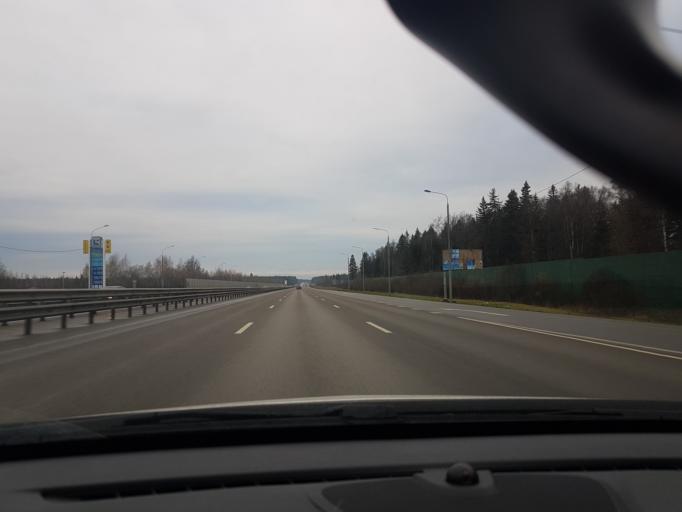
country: RU
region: Moskovskaya
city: Kostrovo
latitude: 55.8572
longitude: 36.7602
